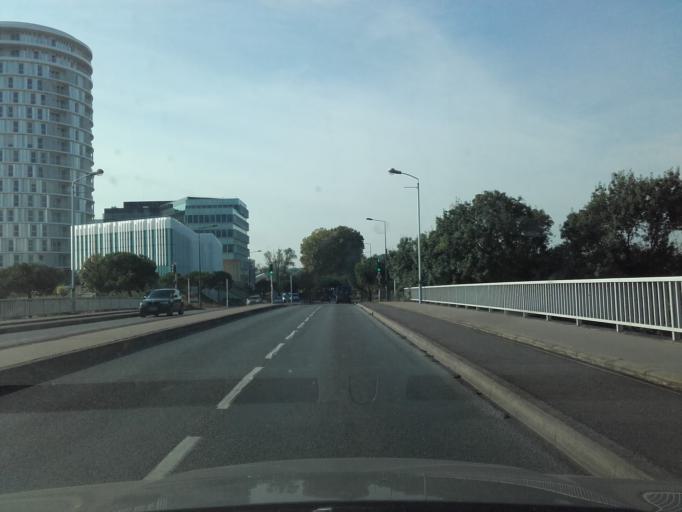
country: FR
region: Centre
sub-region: Departement d'Indre-et-Loire
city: Tours
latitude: 47.3722
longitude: 0.6780
